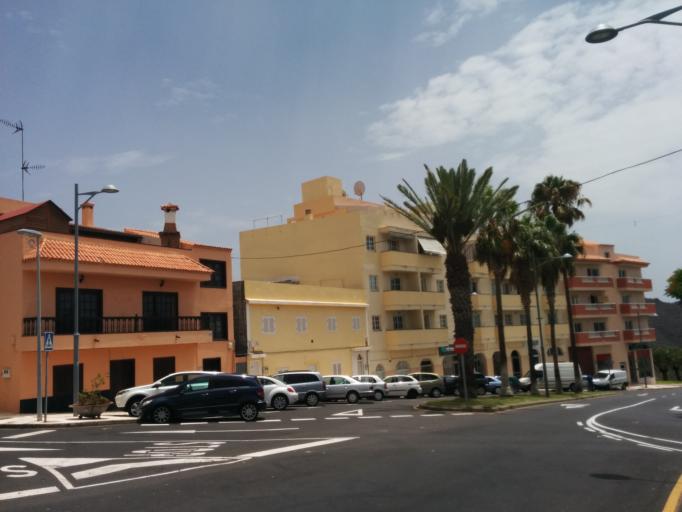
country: ES
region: Canary Islands
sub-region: Provincia de Santa Cruz de Tenerife
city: Adeje
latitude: 28.1192
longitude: -16.7260
